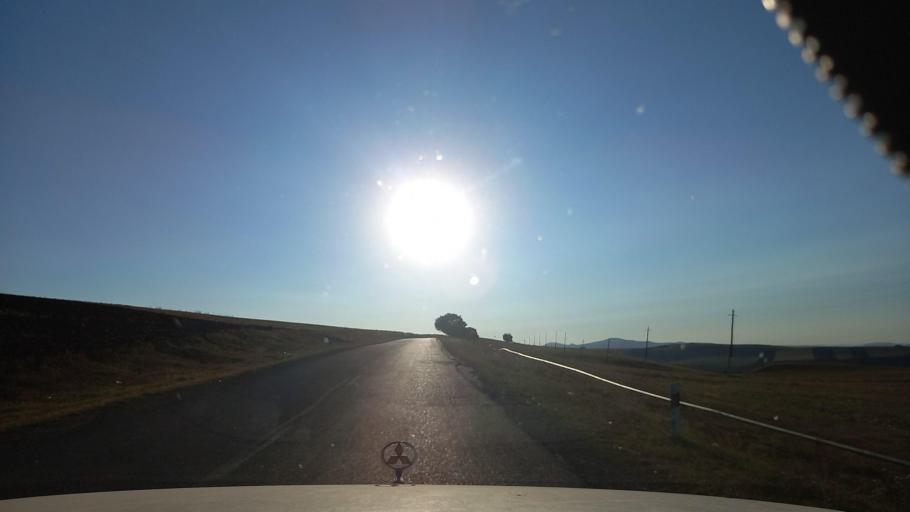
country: AZ
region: Shamkir Rayon
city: Shamkhor
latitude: 40.7659
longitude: 45.9450
